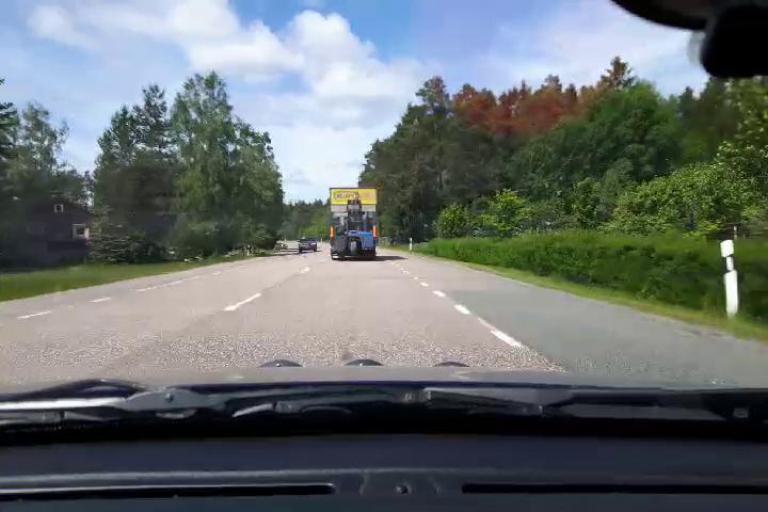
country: SE
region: Uppsala
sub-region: Osthammars Kommun
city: Bjorklinge
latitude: 60.1045
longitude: 17.5487
